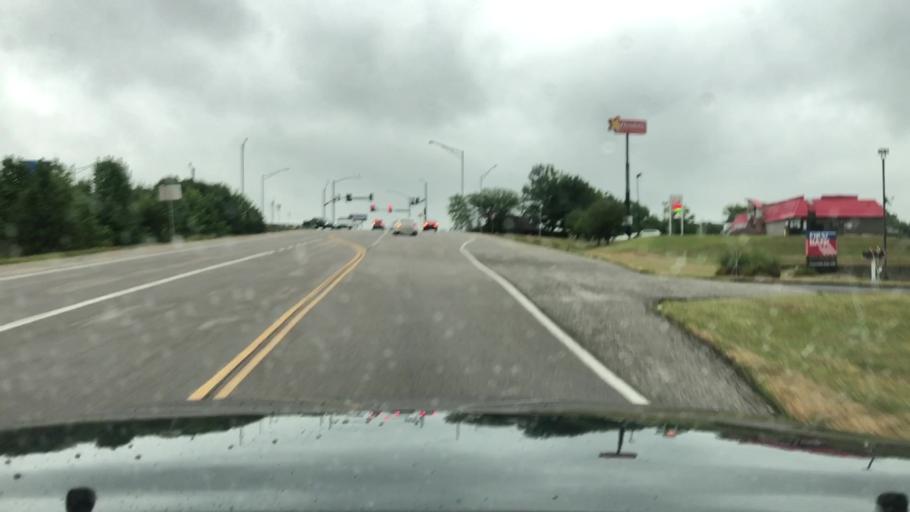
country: US
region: Missouri
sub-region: Saint Charles County
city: Lake Saint Louis
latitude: 38.8034
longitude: -90.7724
